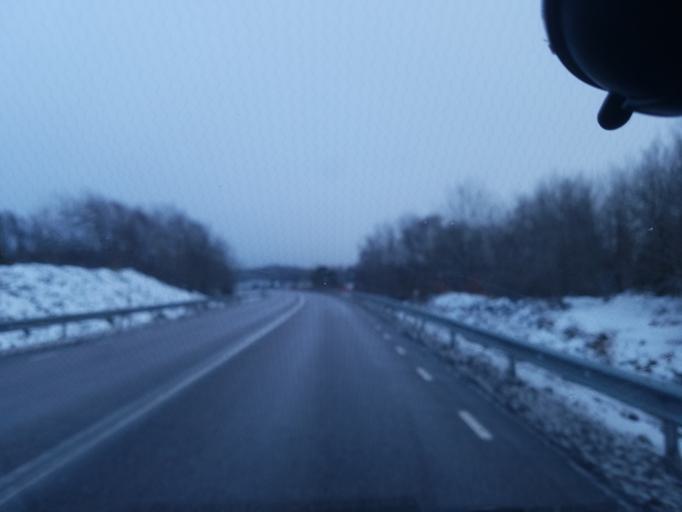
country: SE
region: Vaestra Goetaland
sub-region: Lysekils Kommun
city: Lysekil
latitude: 58.2901
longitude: 11.4643
